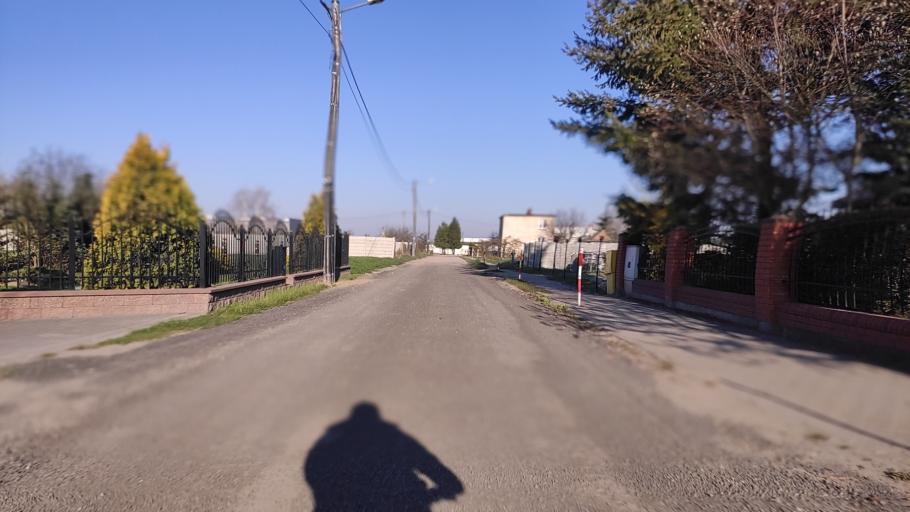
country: PL
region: Greater Poland Voivodeship
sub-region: Powiat poznanski
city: Kleszczewo
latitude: 52.3997
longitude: 17.1527
